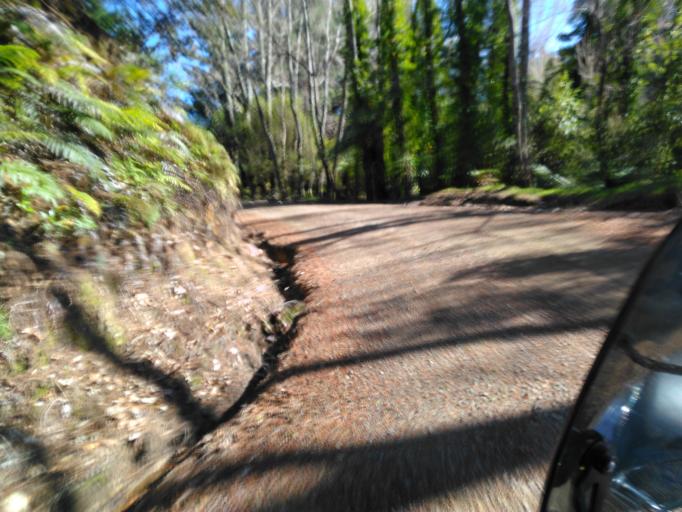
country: NZ
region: Bay of Plenty
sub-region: Opotiki District
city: Opotiki
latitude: -38.3698
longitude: 177.6006
